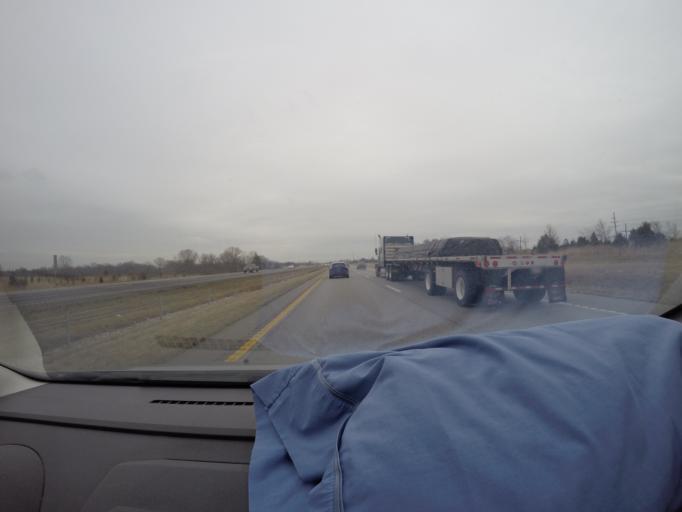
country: US
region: Missouri
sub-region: Warren County
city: Wright City
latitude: 38.8206
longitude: -90.9774
